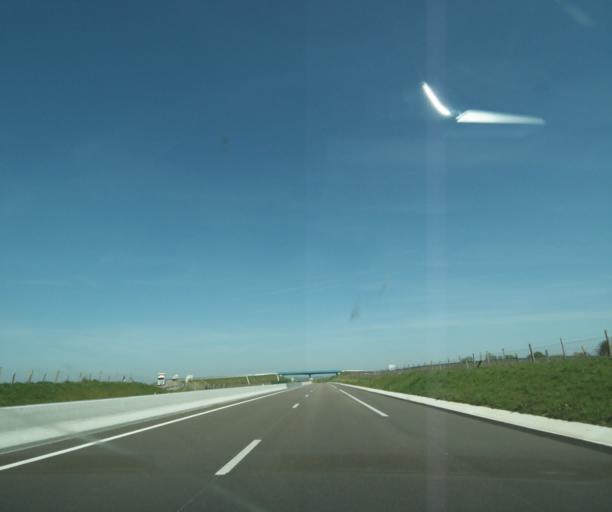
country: FR
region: Bourgogne
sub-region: Departement de la Nievre
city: Saint-Pierre-le-Moutier
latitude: 46.8157
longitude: 3.1237
